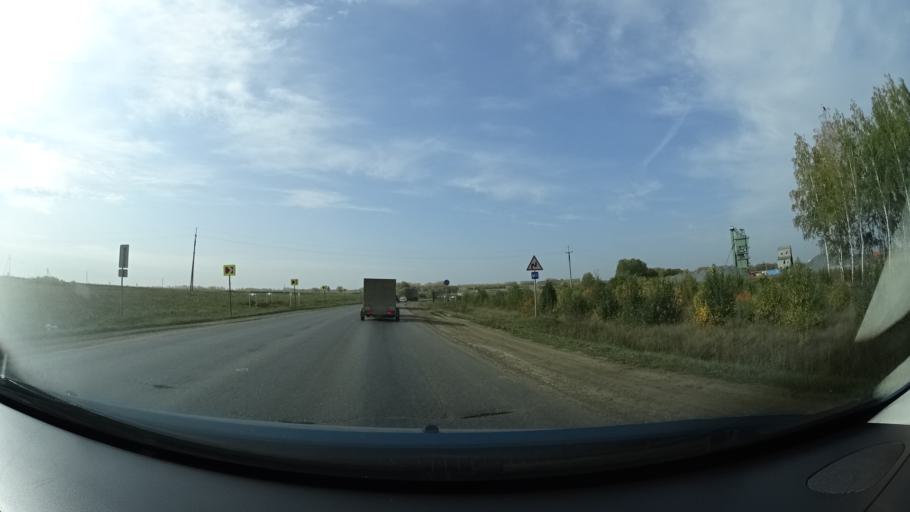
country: RU
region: Bashkortostan
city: Buzdyak
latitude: 54.6265
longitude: 54.4560
